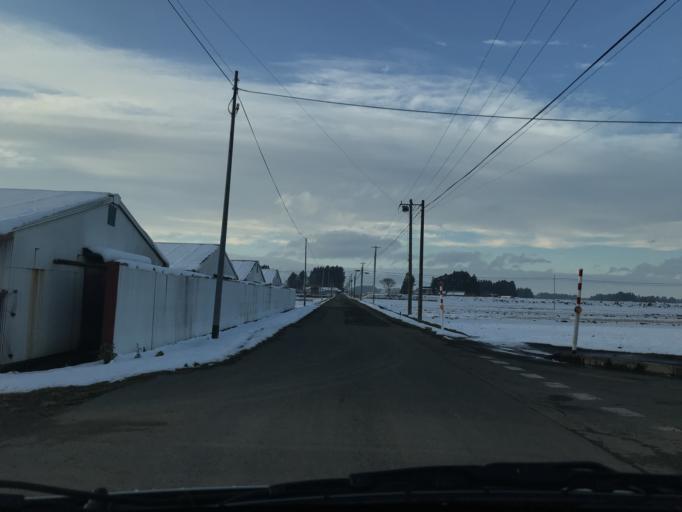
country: JP
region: Iwate
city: Mizusawa
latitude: 39.0529
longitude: 141.0973
